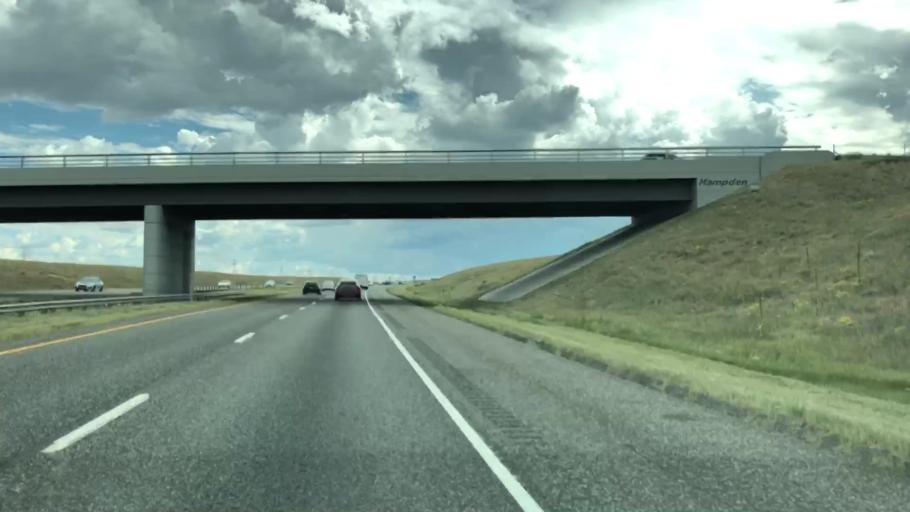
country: US
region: Colorado
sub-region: Arapahoe County
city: Dove Valley
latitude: 39.6538
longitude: -104.7201
